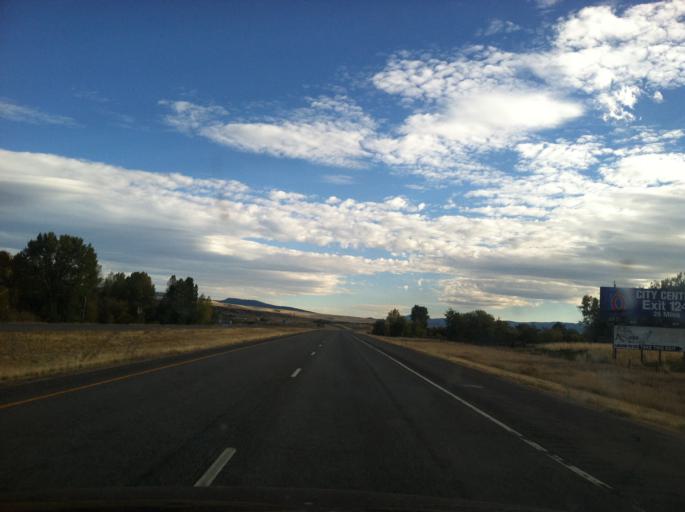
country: US
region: Montana
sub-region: Deer Lodge County
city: Warm Springs
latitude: 46.2783
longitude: -112.7475
